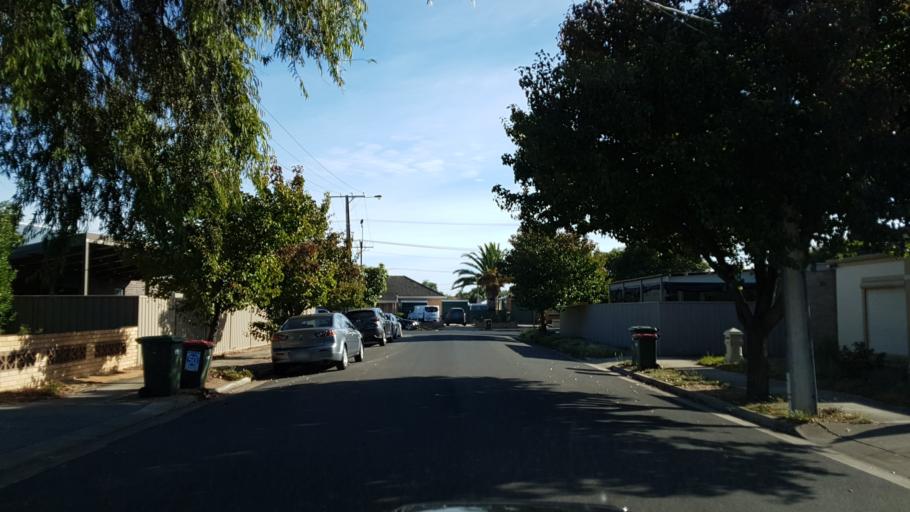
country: AU
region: South Australia
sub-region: City of West Torrens
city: Plympton
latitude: -34.9521
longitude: 138.5479
